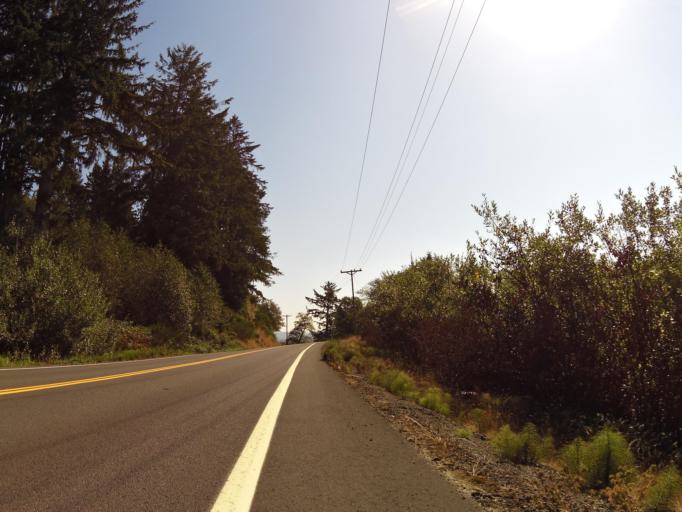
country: US
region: Oregon
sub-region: Tillamook County
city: Pacific City
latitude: 45.1828
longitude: -123.9451
